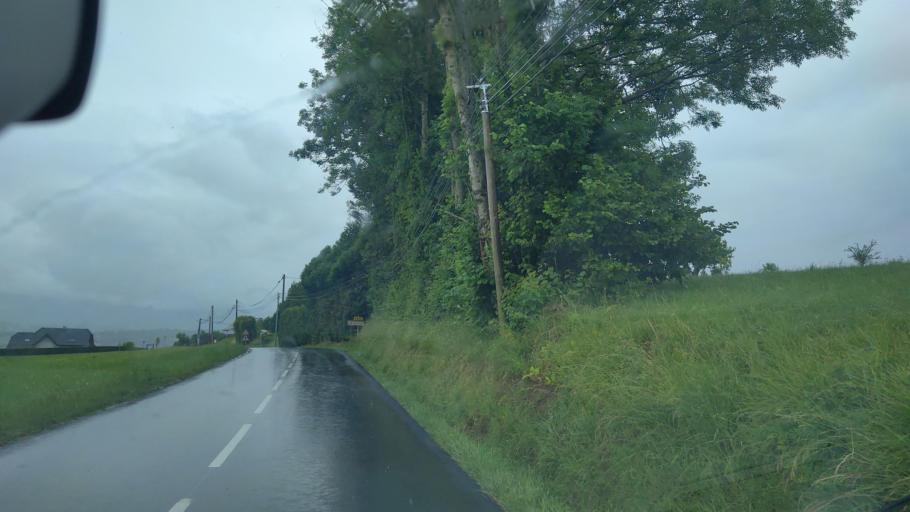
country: FR
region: Rhone-Alpes
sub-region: Departement de la Savoie
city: La Biolle
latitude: 45.7619
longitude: 5.9245
